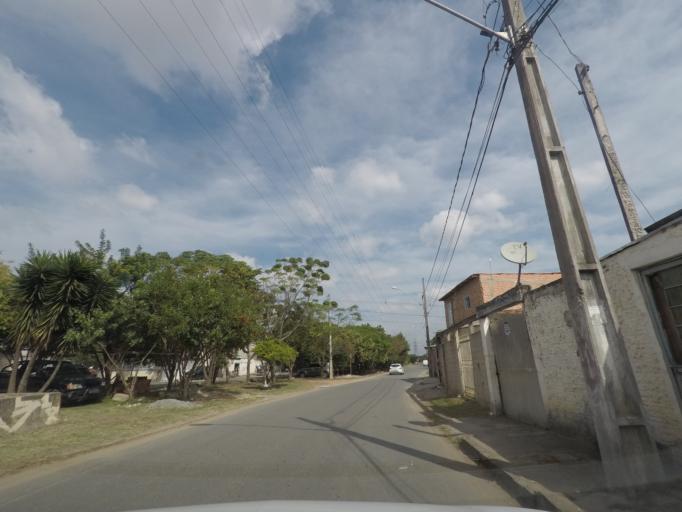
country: BR
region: Parana
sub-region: Pinhais
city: Pinhais
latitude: -25.4638
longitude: -49.1963
